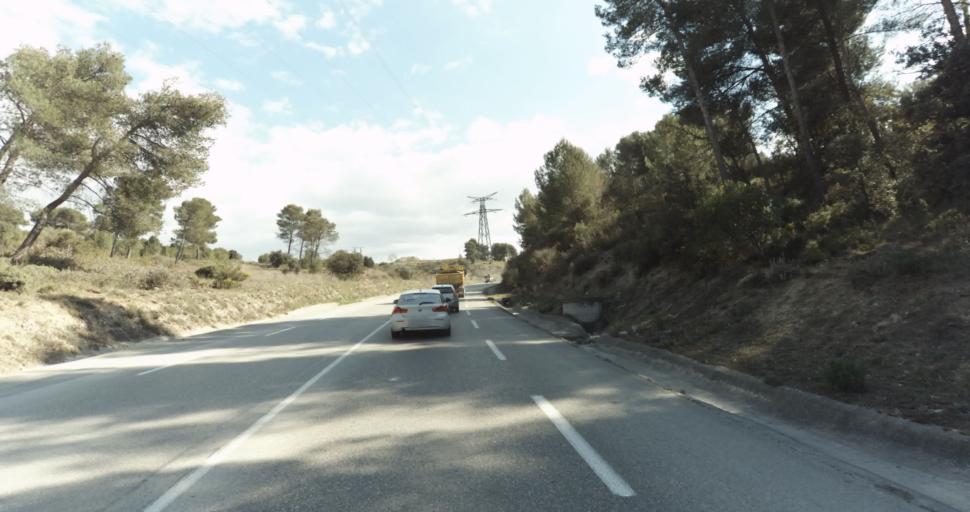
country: FR
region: Provence-Alpes-Cote d'Azur
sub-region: Departement des Bouches-du-Rhone
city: Gardanne
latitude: 43.4574
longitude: 5.4919
